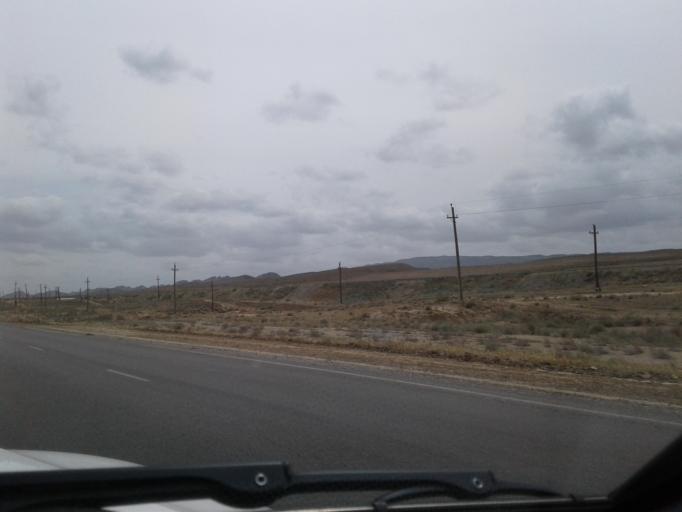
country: IR
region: Razavi Khorasan
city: Dargaz
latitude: 37.6532
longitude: 59.1242
